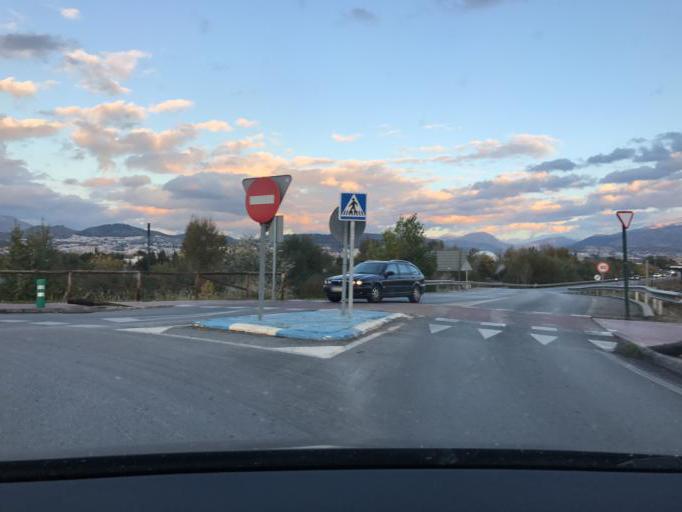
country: ES
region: Andalusia
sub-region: Provincia de Granada
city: Armilla
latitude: 37.1630
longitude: -3.6281
